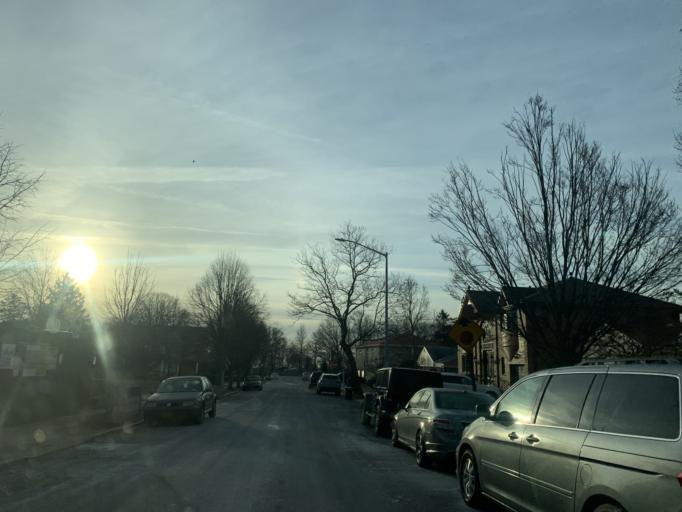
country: US
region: New York
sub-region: Nassau County
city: Lake Success
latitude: 40.7555
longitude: -73.7248
